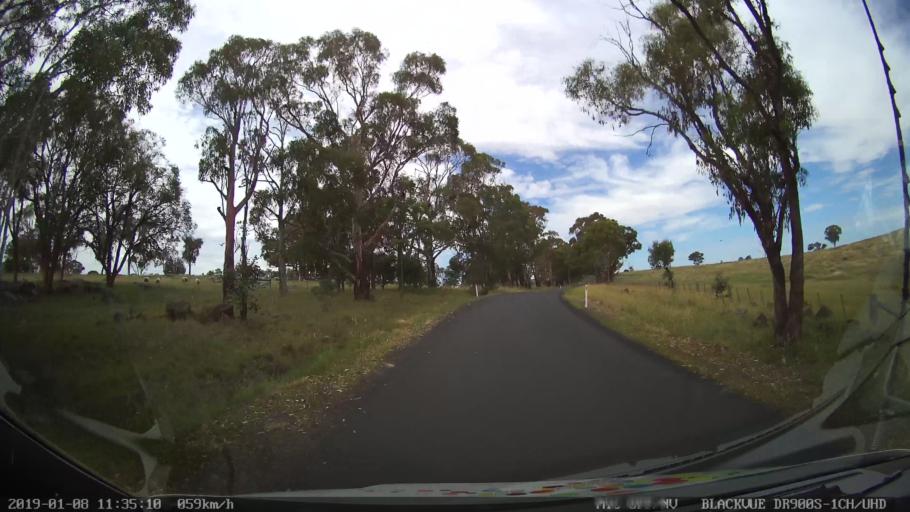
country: AU
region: New South Wales
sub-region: Guyra
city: Guyra
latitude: -30.3345
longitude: 151.5377
